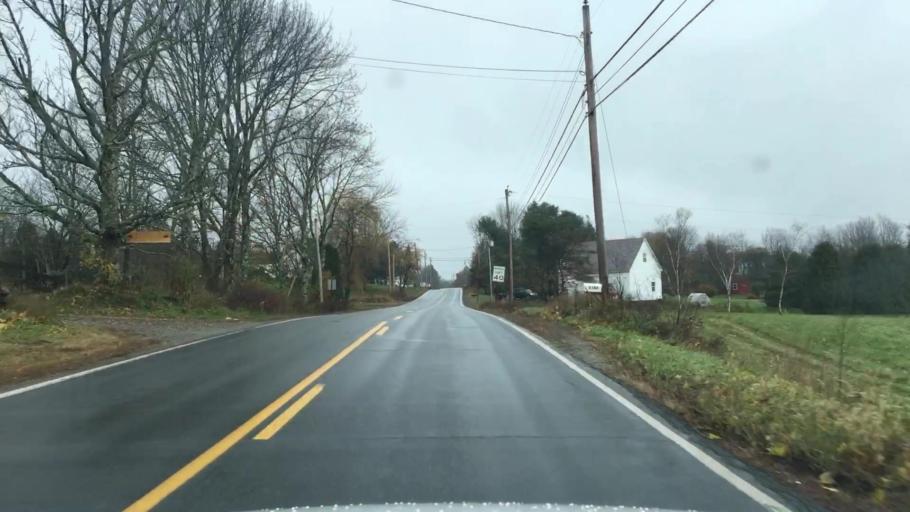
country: US
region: Maine
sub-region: Lincoln County
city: Jefferson
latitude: 44.1576
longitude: -69.4165
